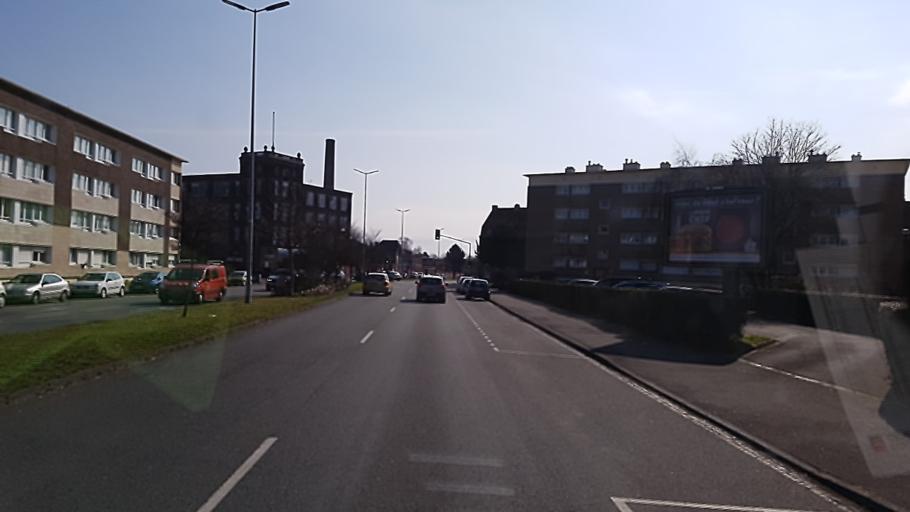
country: FR
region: Nord-Pas-de-Calais
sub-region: Departement du Nord
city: Tourcoing
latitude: 50.7359
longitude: 3.1738
